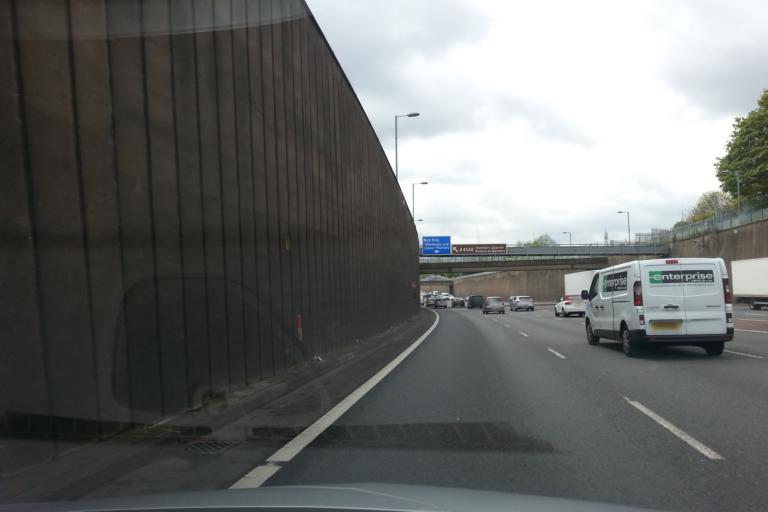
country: GB
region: England
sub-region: City and Borough of Birmingham
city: Birmingham
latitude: 52.5009
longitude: -1.8849
